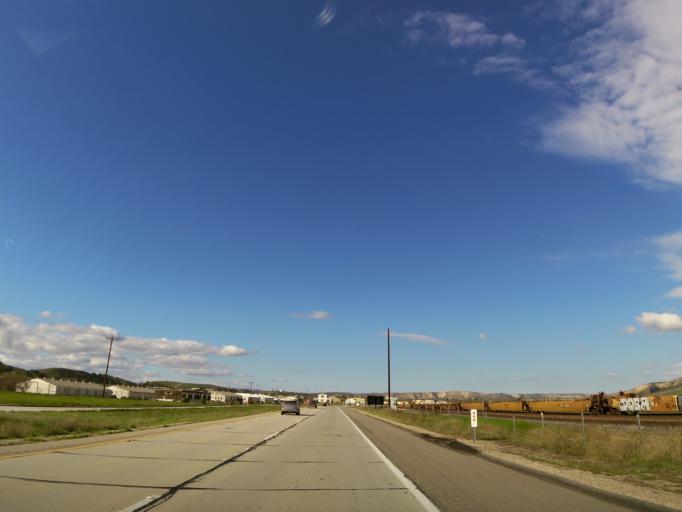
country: US
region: California
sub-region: San Luis Obispo County
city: San Miguel
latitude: 35.7798
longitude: -120.7200
